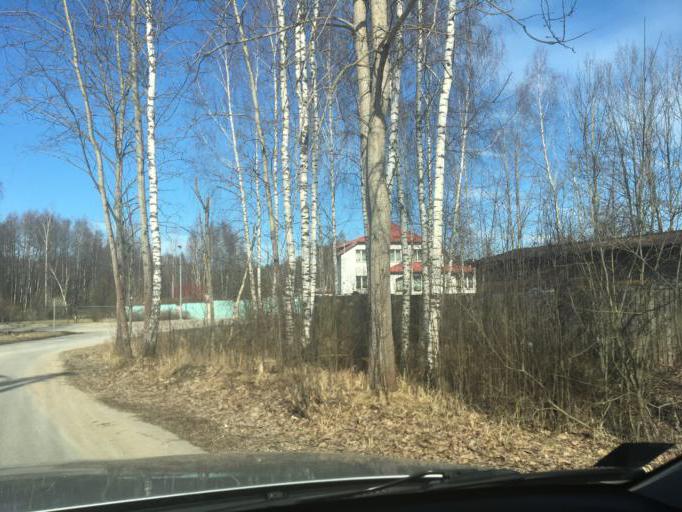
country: LV
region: Stopini
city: Ulbroka
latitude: 56.9309
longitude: 24.3081
